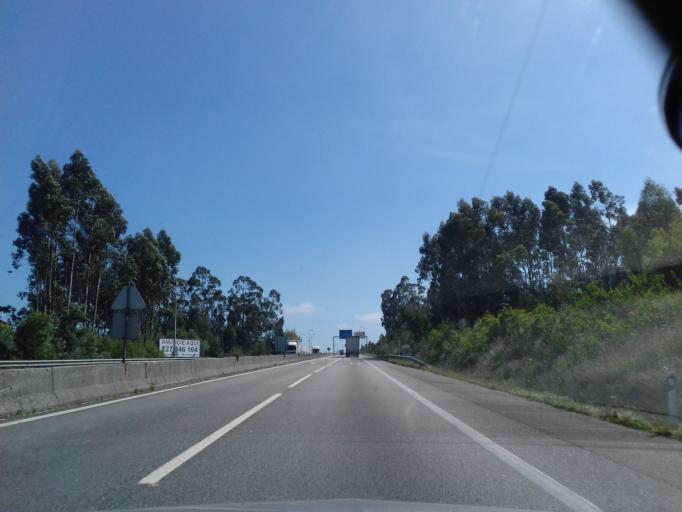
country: PT
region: Aveiro
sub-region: Espinho
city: Souto
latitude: 40.9771
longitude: -8.6107
